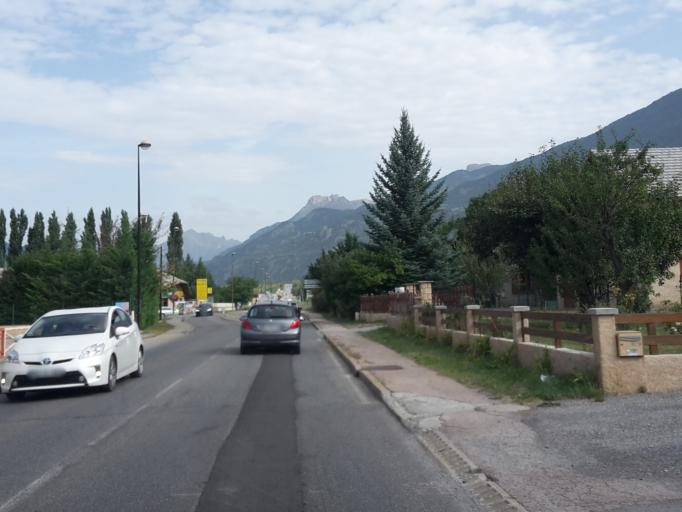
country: FR
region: Provence-Alpes-Cote d'Azur
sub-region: Departement des Hautes-Alpes
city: Guillestre
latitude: 44.6750
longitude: 6.6171
